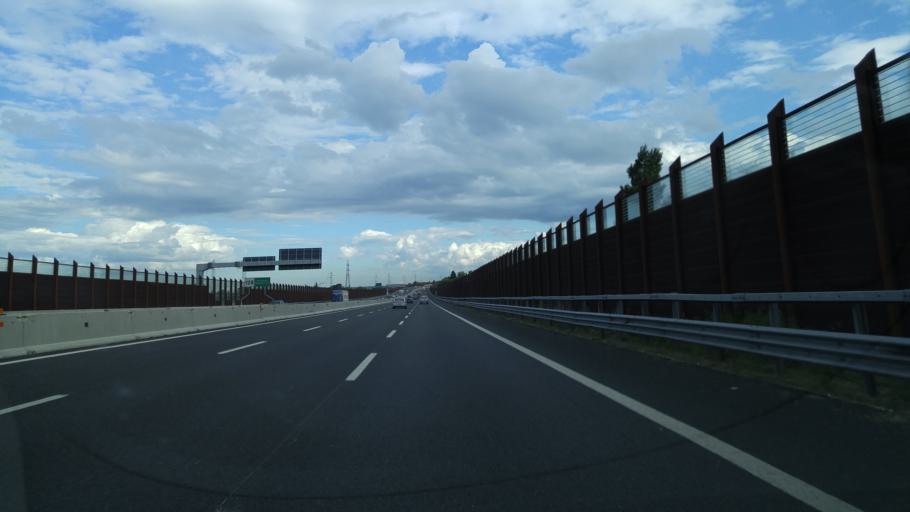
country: IT
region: Emilia-Romagna
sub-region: Provincia di Rimini
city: Rimini
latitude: 44.0324
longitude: 12.5731
